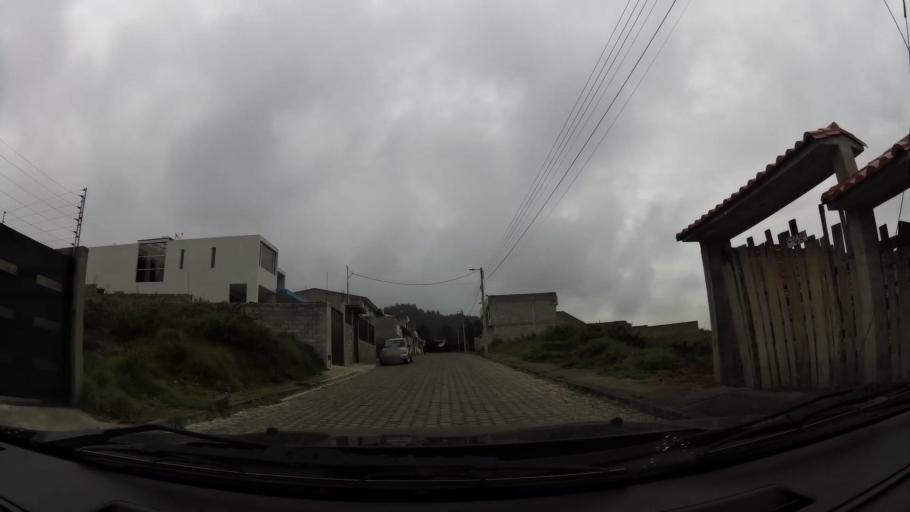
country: EC
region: Pichincha
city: Quito
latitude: -0.2656
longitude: -78.4765
